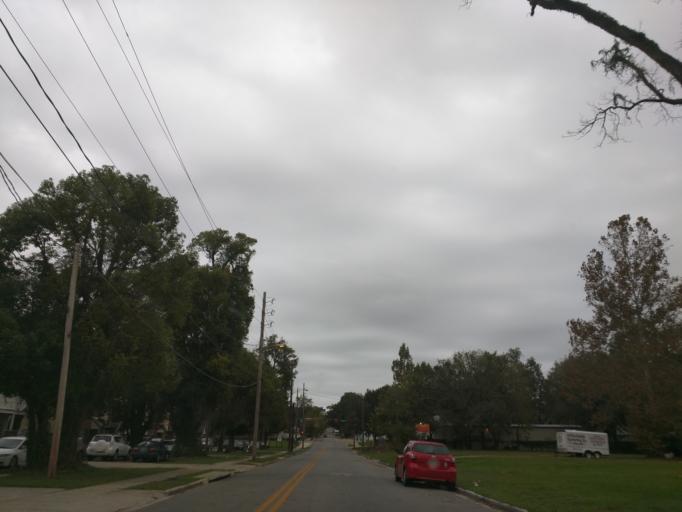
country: US
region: Florida
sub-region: Leon County
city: Tallahassee
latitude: 30.4458
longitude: -84.2903
